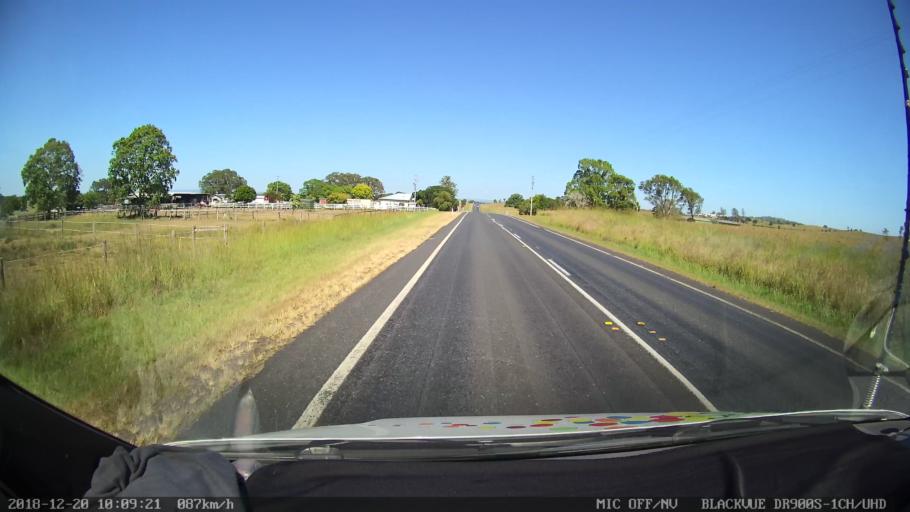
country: AU
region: New South Wales
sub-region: Lismore Municipality
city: Lismore
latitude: -28.8774
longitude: 153.1889
